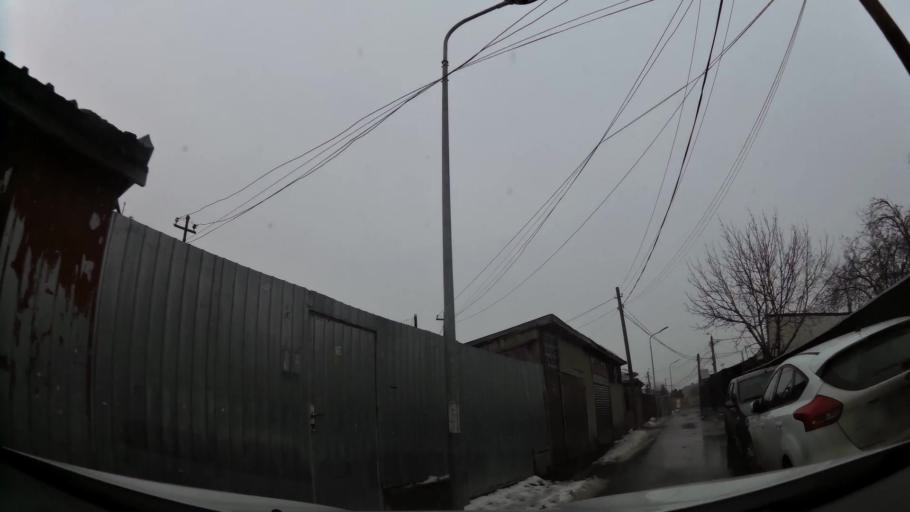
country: RO
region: Ilfov
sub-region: Comuna Magurele
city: Magurele
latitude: 44.3819
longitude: 26.0442
